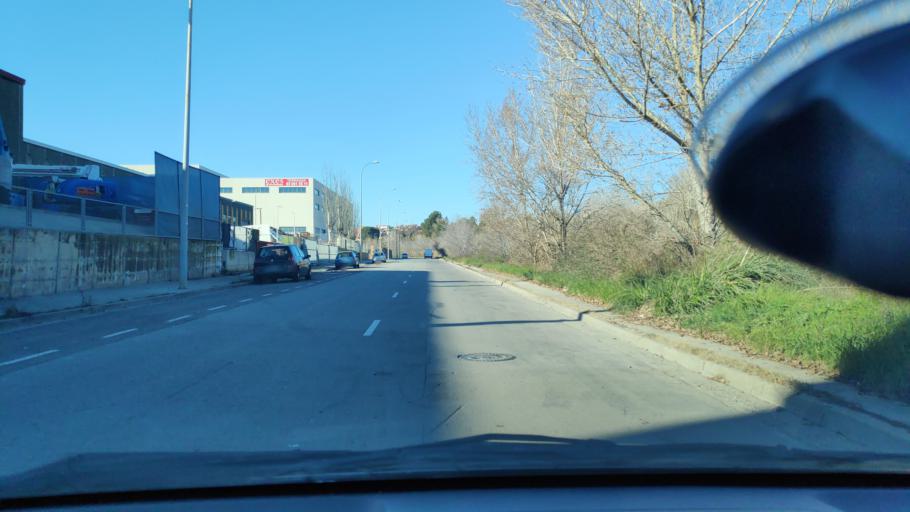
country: ES
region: Catalonia
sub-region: Provincia de Barcelona
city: Sant Quirze del Valles
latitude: 41.5231
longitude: 2.0949
